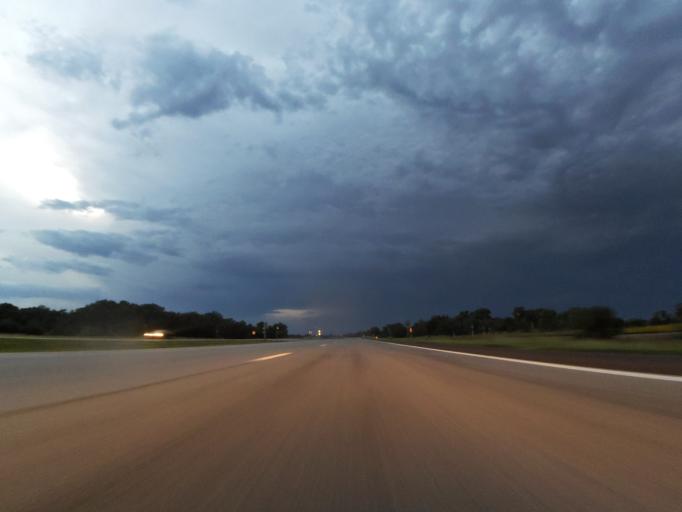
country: US
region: Kansas
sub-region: Reno County
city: South Hutchinson
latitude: 37.9641
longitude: -97.9205
